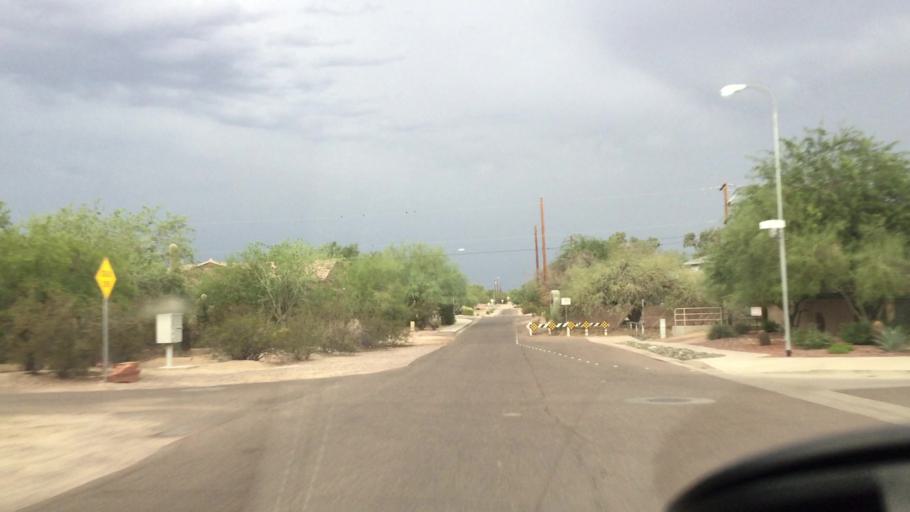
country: US
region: Arizona
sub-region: Maricopa County
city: Guadalupe
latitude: 33.3669
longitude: -112.0369
